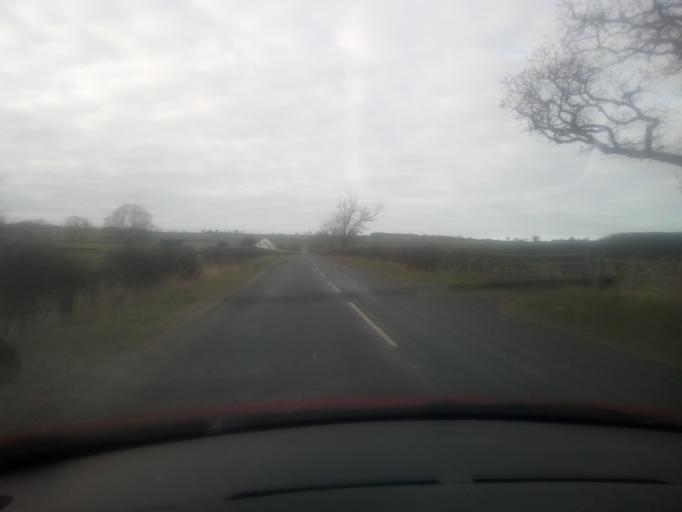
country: GB
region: England
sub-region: Darlington
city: Summerhouse
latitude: 54.5819
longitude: -1.6787
